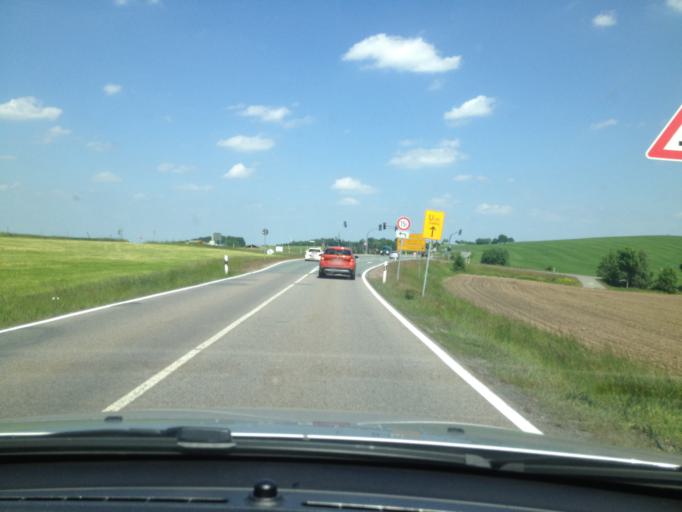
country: DE
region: Saxony
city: Burkhardtsdorf
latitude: 50.7465
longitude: 12.9285
